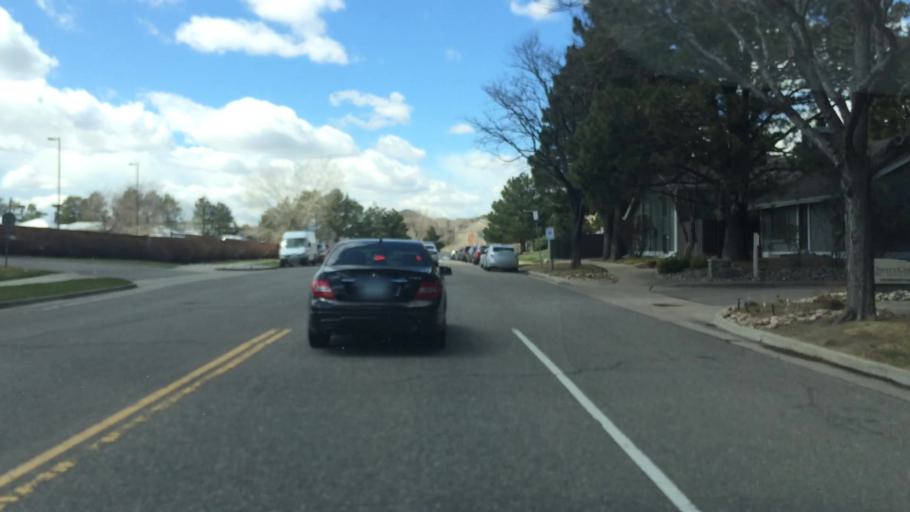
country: US
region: Colorado
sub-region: Arapahoe County
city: Centennial
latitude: 39.5972
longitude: -104.8712
